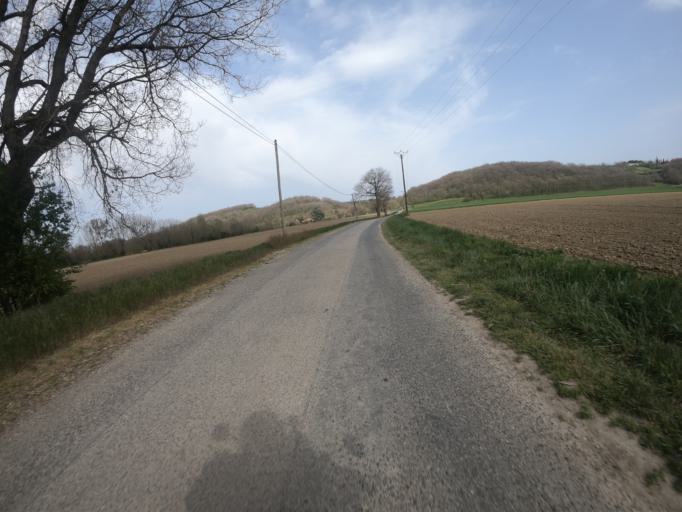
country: FR
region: Languedoc-Roussillon
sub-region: Departement de l'Aude
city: Belpech
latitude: 43.1727
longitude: 1.7332
